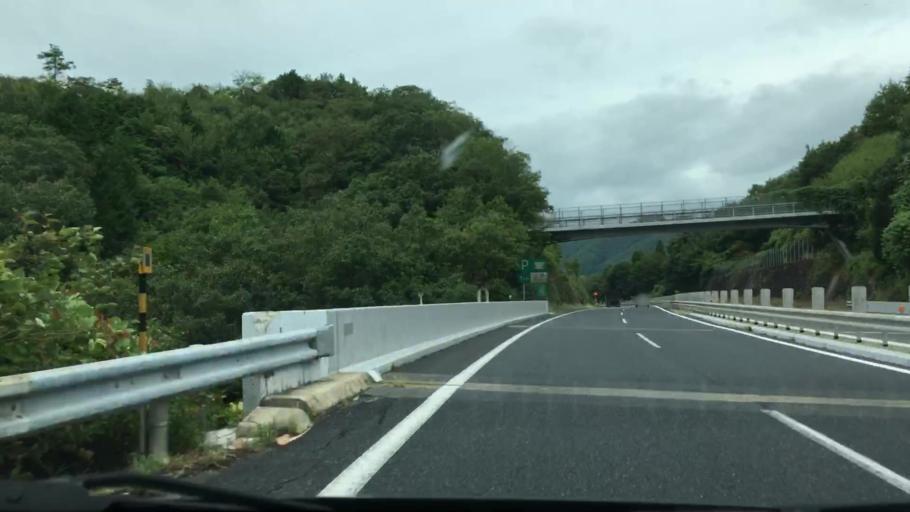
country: JP
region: Hyogo
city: Yamazakicho-nakabirose
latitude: 35.0074
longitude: 134.3219
